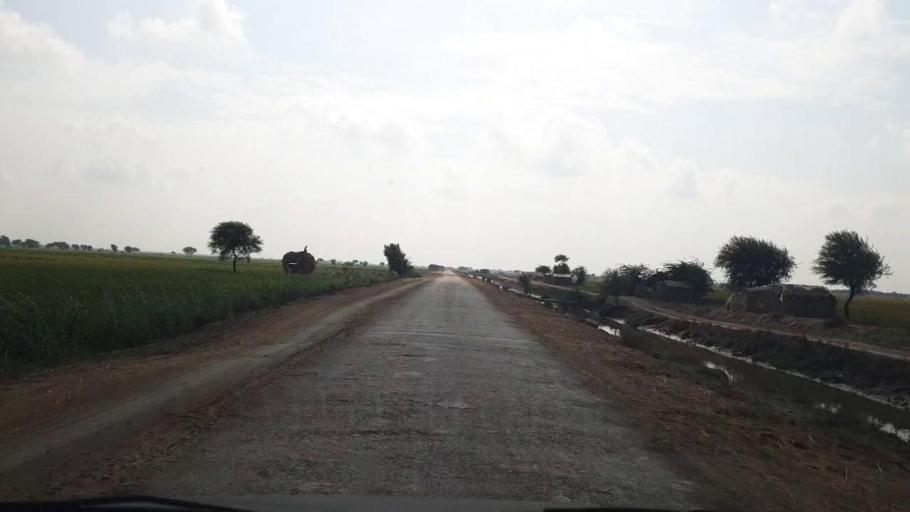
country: PK
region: Sindh
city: Kario
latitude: 24.5856
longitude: 68.5757
